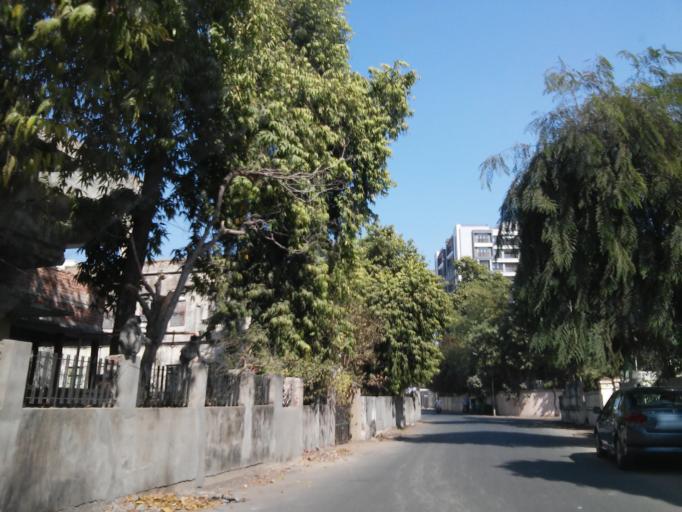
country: IN
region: Gujarat
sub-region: Ahmadabad
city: Ahmedabad
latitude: 23.0128
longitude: 72.5575
